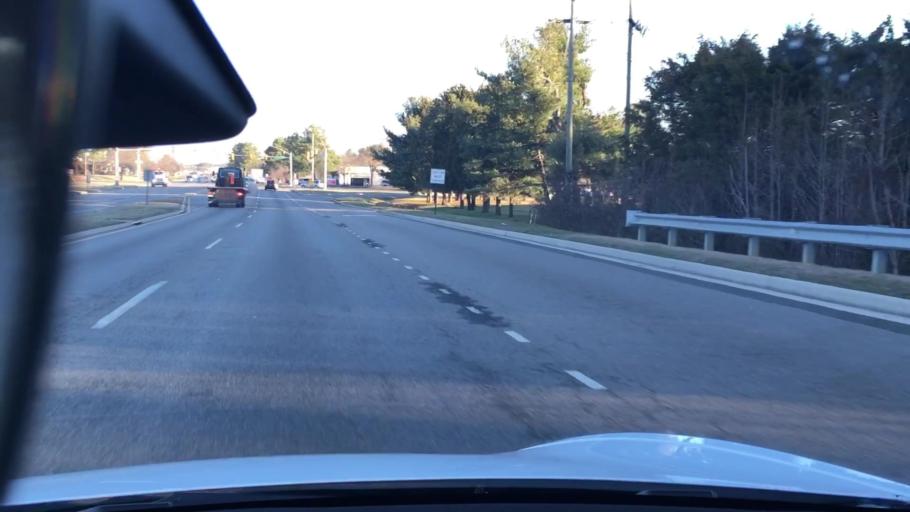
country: US
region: Virginia
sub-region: Henrico County
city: Fort Lee
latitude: 37.5022
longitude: -77.3495
